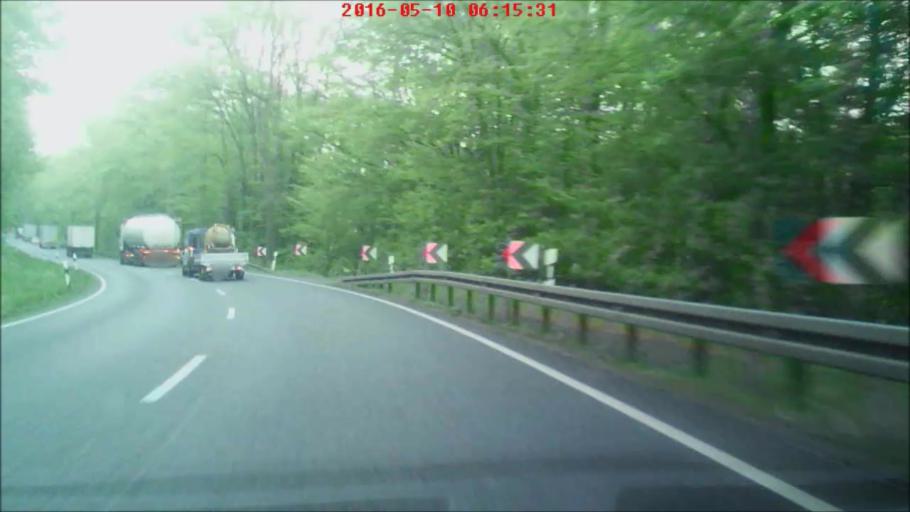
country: DE
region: Hesse
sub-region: Regierungsbezirk Kassel
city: Burghaun
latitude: 50.7511
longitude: 9.6835
